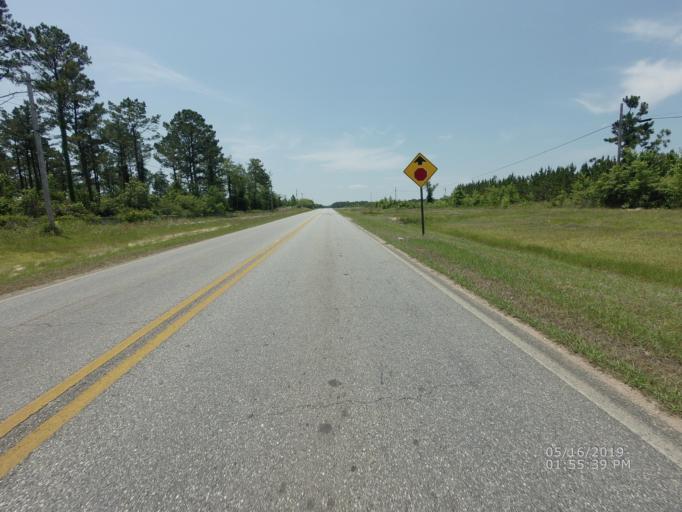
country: US
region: Georgia
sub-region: Dougherty County
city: Albany
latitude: 31.5490
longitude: -84.2500
